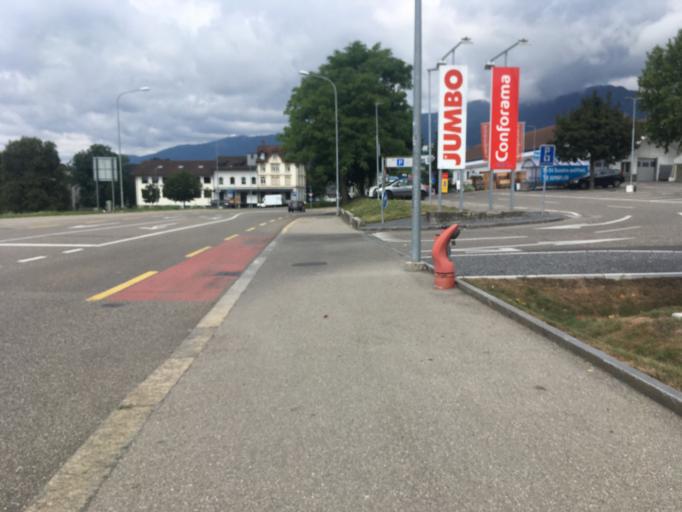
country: CH
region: Solothurn
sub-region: Bezirk Solothurn
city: Solothurn
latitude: 47.2105
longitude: 7.5280
